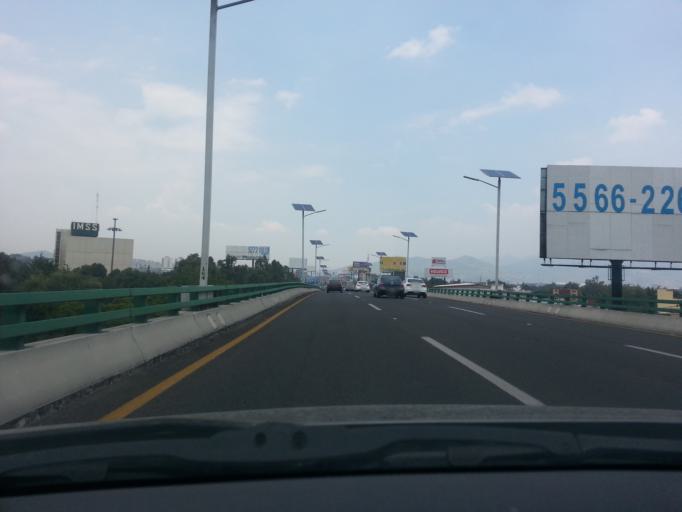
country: MX
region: Mexico
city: Vista Hermosa
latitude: 19.5288
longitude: -99.2229
